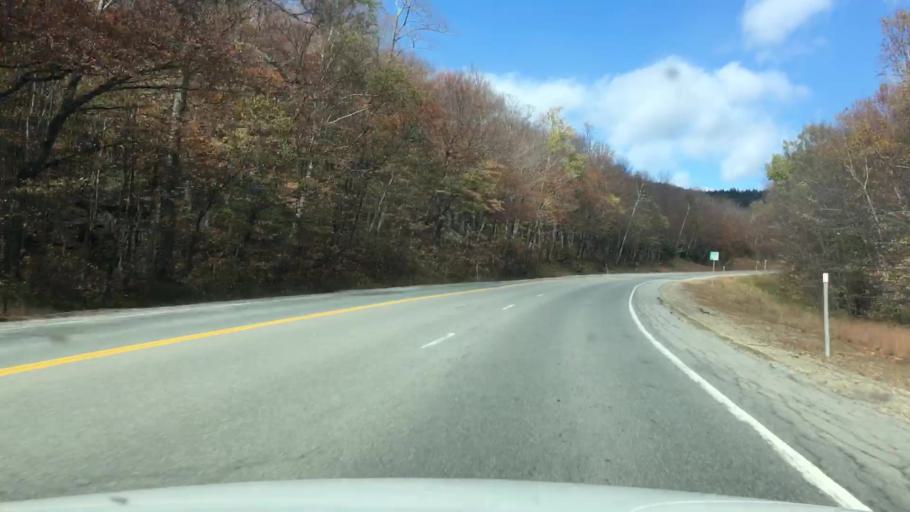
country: US
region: New Hampshire
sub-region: Coos County
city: Gorham
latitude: 44.2340
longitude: -71.2574
